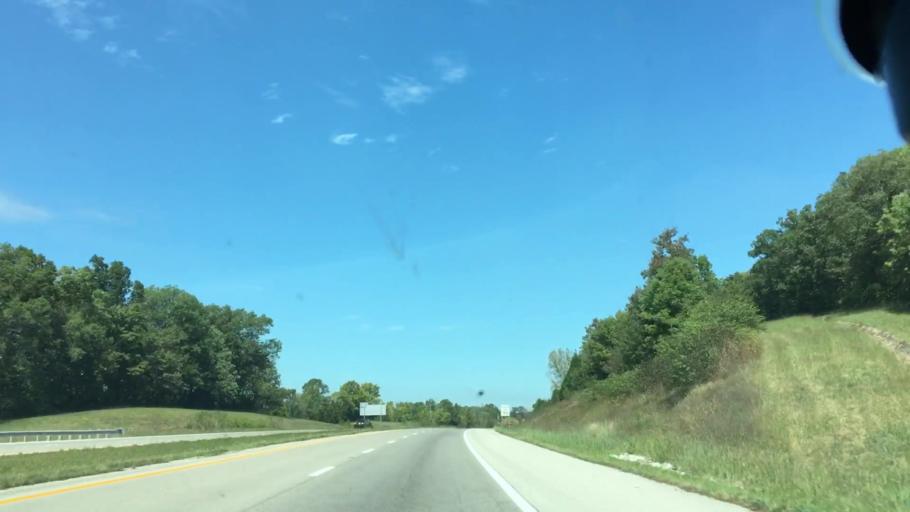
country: US
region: Kentucky
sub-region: Christian County
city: Hopkinsville
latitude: 36.9059
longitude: -87.4729
